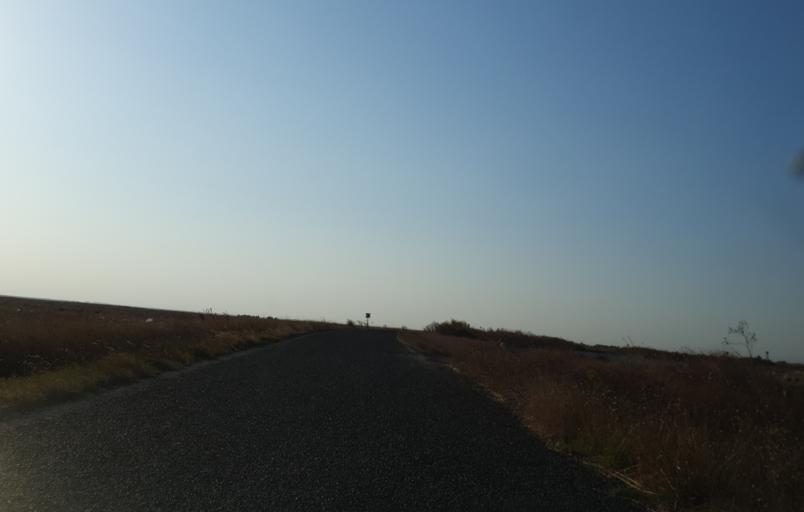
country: TR
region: Tekirdag
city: Beyazkoy
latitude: 41.4202
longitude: 27.7632
